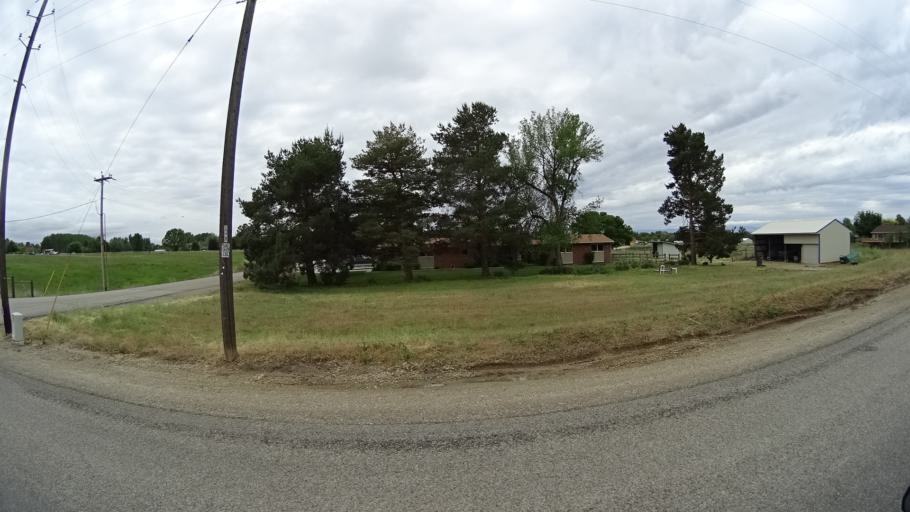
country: US
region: Idaho
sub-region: Ada County
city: Eagle
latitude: 43.7353
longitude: -116.3797
